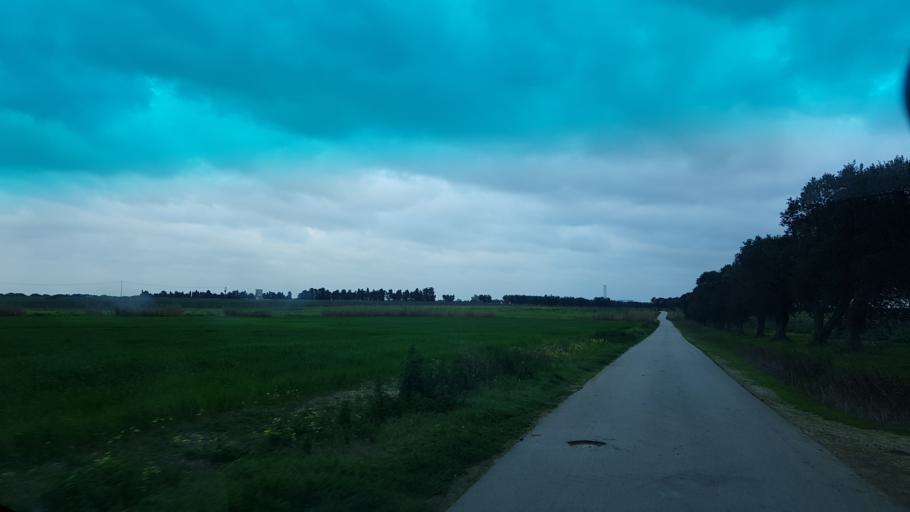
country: IT
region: Apulia
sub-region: Provincia di Brindisi
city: La Rosa
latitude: 40.5951
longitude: 17.9736
